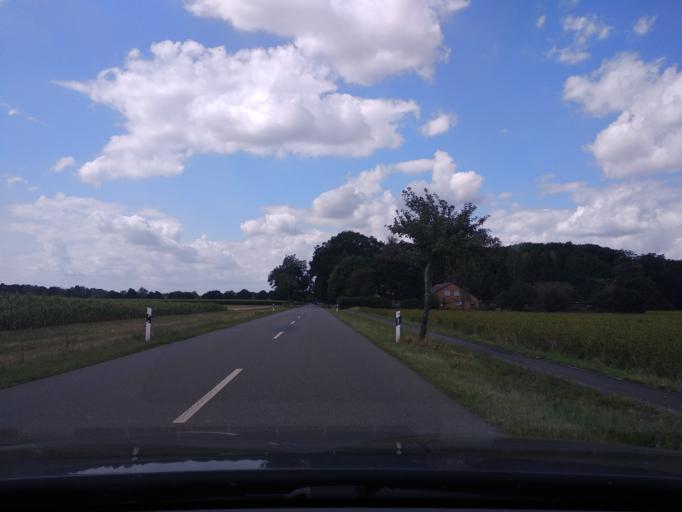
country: DE
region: Lower Saxony
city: Wagenhoff
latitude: 52.5088
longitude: 10.5096
